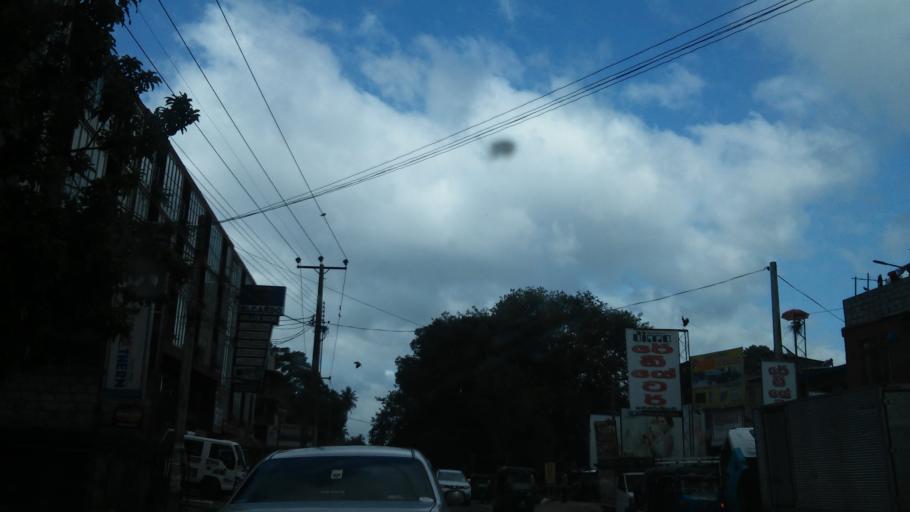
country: LK
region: Central
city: Kandy
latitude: 7.2823
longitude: 80.6238
